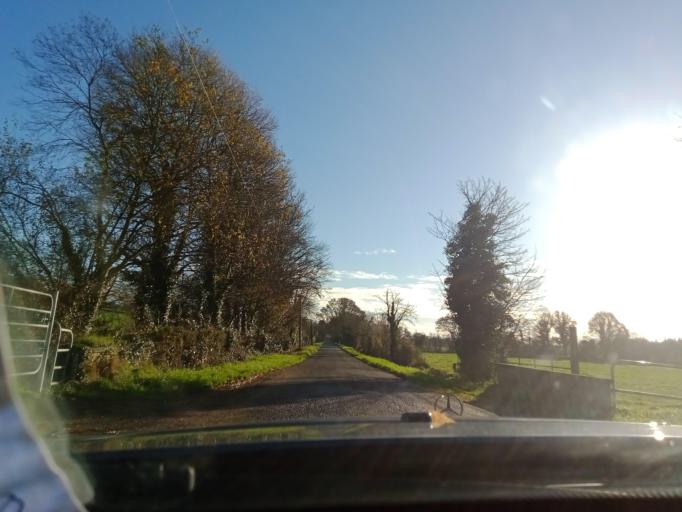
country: IE
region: Leinster
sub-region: Kilkenny
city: Piltown
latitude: 52.3482
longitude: -7.2804
